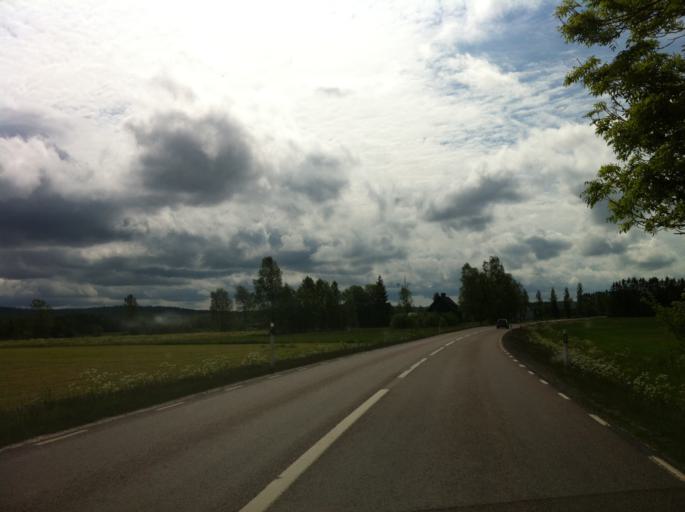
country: SE
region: Vaermland
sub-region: Sunne Kommun
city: Sunne
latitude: 59.6708
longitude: 13.1496
